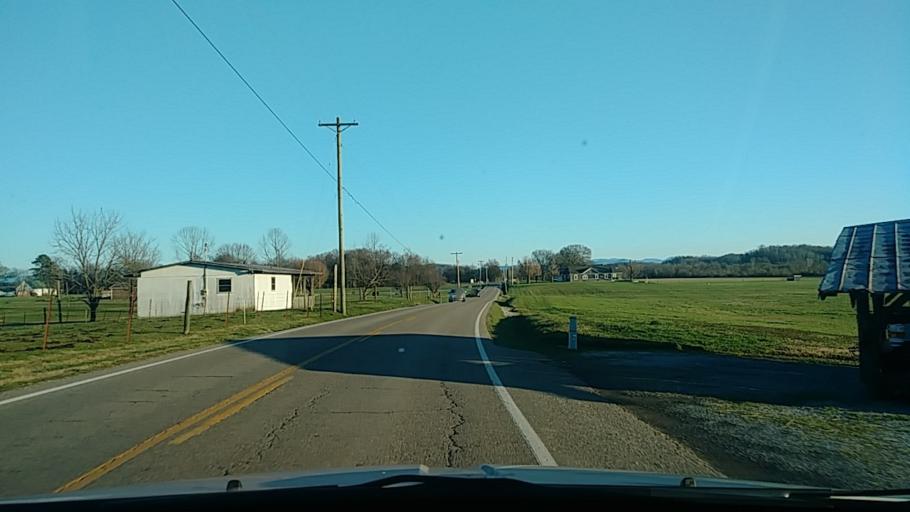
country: US
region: Tennessee
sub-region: Jefferson County
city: White Pine
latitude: 36.1483
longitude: -83.1493
